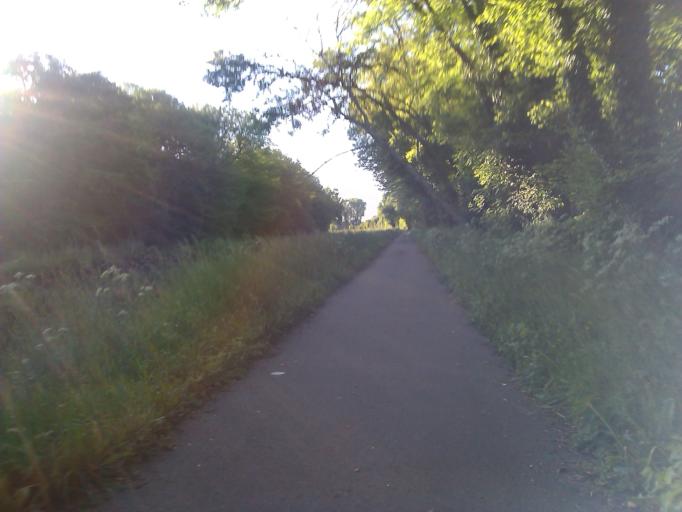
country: FR
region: Auvergne
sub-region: Departement de l'Allier
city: Dompierre-sur-Besbre
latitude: 46.5347
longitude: 3.7150
